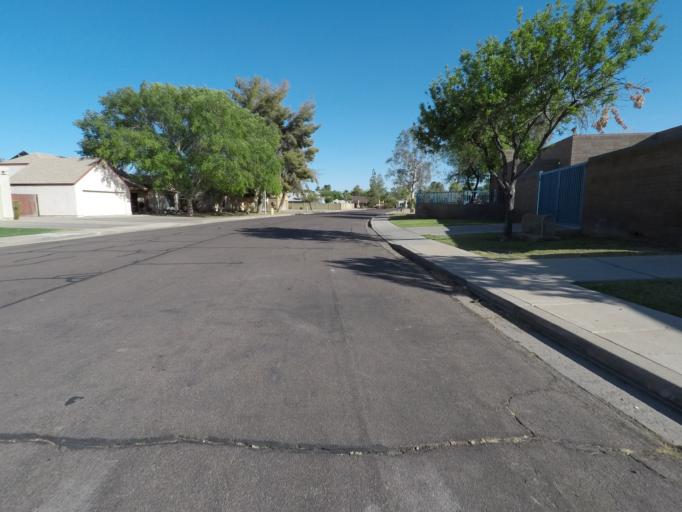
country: US
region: Arizona
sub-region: Maricopa County
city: Guadalupe
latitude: 33.3547
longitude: -111.9193
